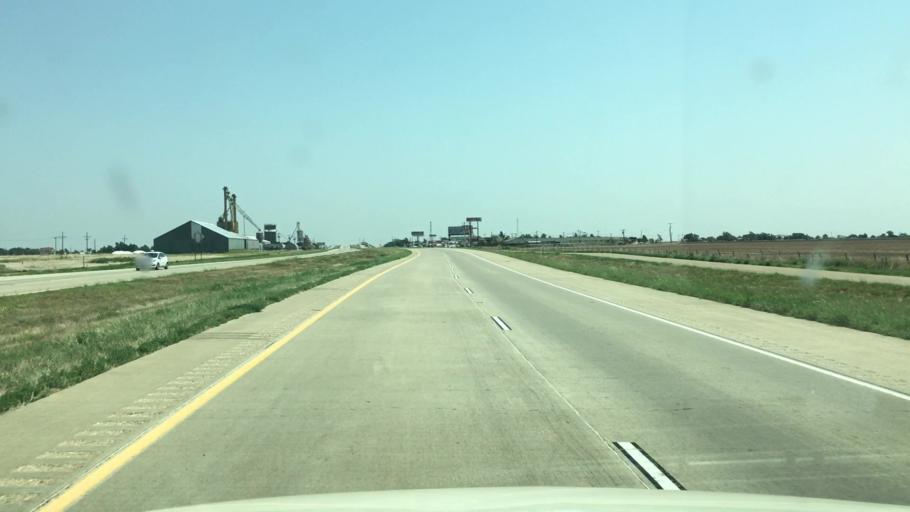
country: US
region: Texas
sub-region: Potter County
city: Bushland
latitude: 35.2096
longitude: -102.2158
